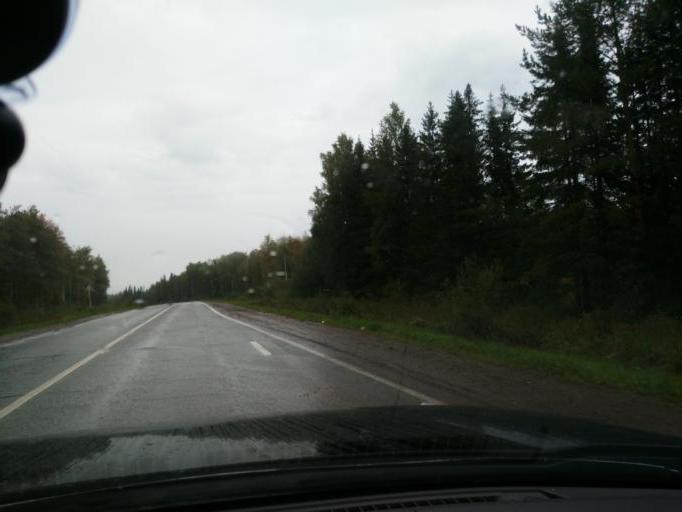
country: RU
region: Perm
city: Yugo-Kamskiy
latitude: 57.4978
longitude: 55.6873
